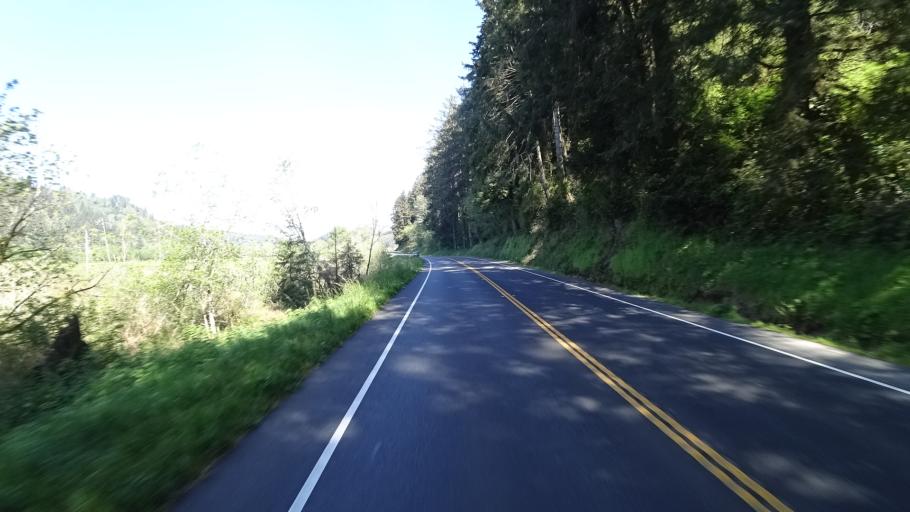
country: US
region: California
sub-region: Del Norte County
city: Bertsch-Oceanview
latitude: 41.5493
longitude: -124.0528
